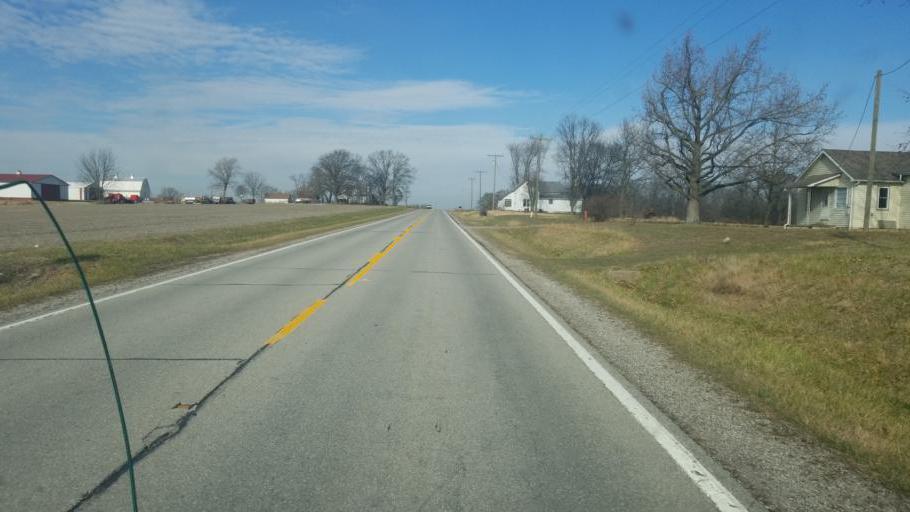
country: US
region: Illinois
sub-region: Saline County
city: Eldorado
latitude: 37.9236
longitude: -88.4576
